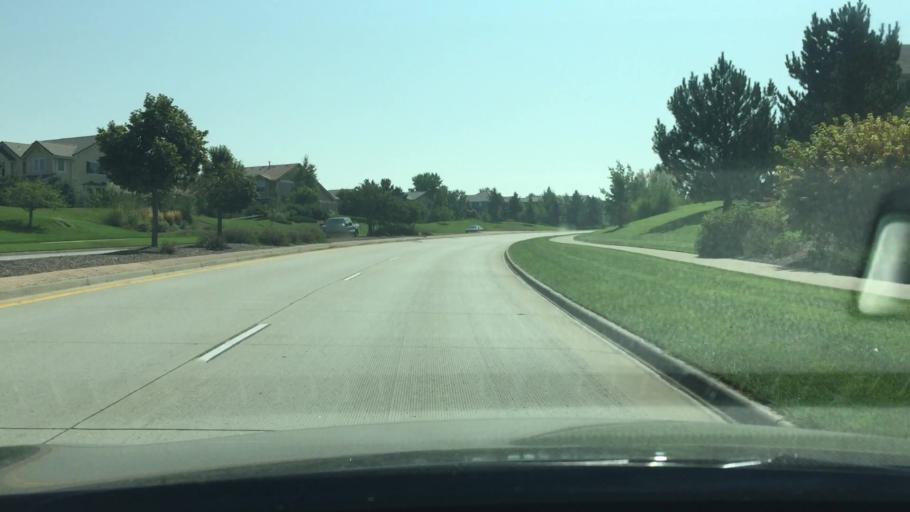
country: US
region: Colorado
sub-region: Arapahoe County
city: Dove Valley
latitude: 39.6065
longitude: -104.7890
